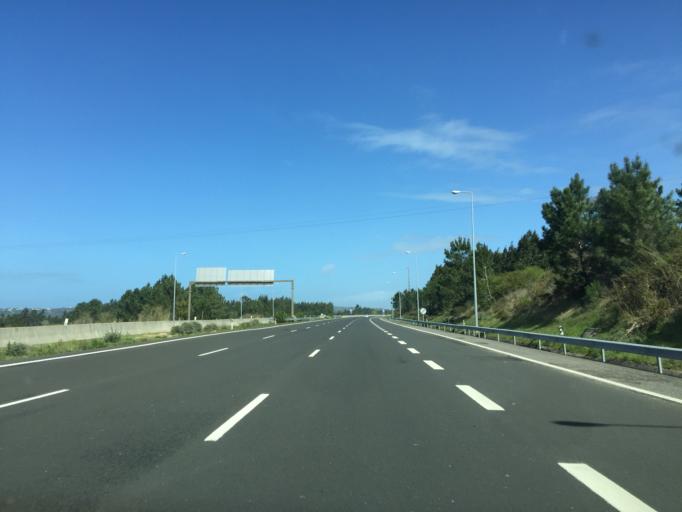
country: PT
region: Leiria
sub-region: Nazare
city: Nazare
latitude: 39.5053
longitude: -9.0901
